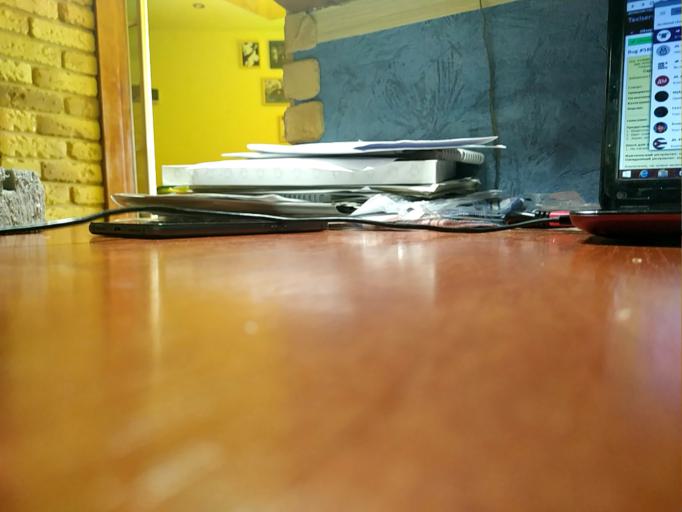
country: RU
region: Vologda
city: Khokhlovo
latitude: 59.4226
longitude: 37.3420
